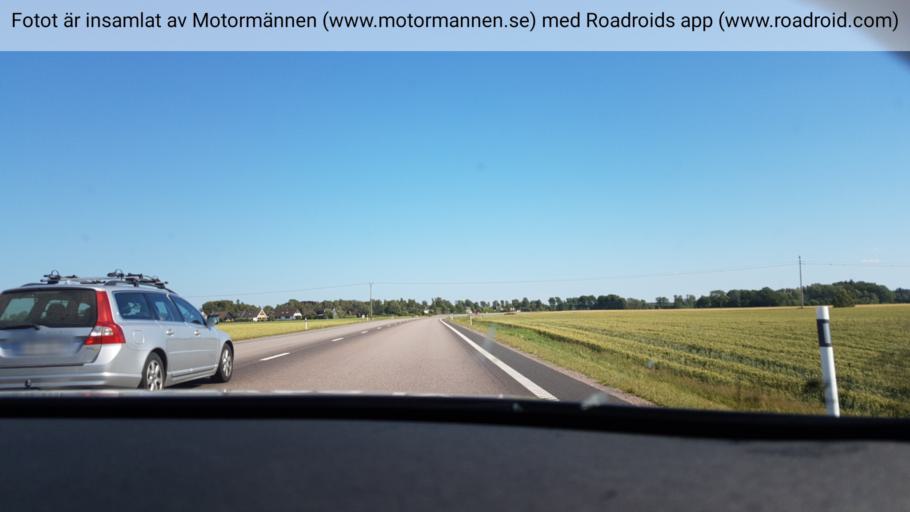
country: SE
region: Vaestra Goetaland
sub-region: Skara Kommun
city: Skara
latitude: 58.3947
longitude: 13.4058
